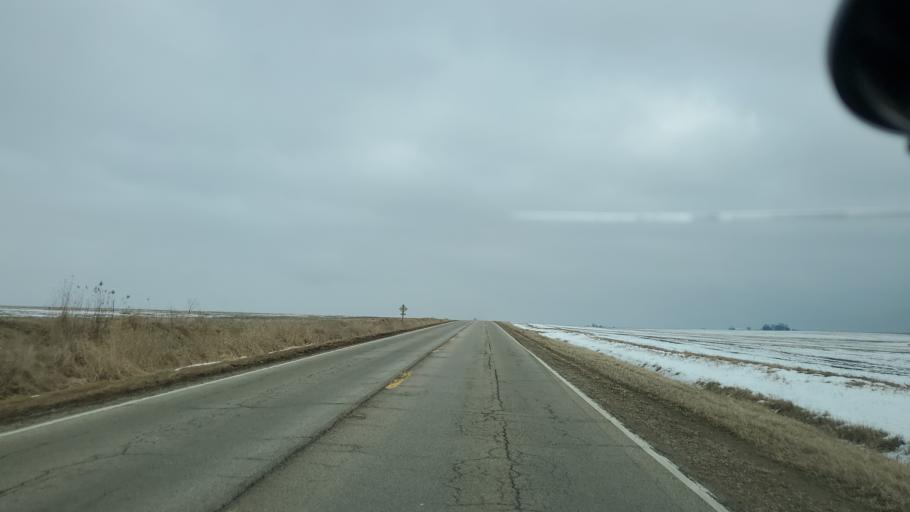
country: US
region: Illinois
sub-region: Marshall County
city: Wenona
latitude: 41.1187
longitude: -89.1419
